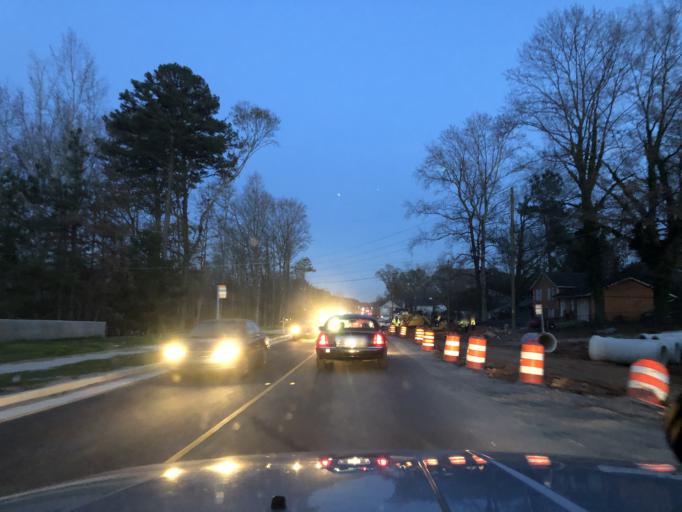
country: US
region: Georgia
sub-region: Clayton County
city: Jonesboro
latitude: 33.5181
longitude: -84.3874
